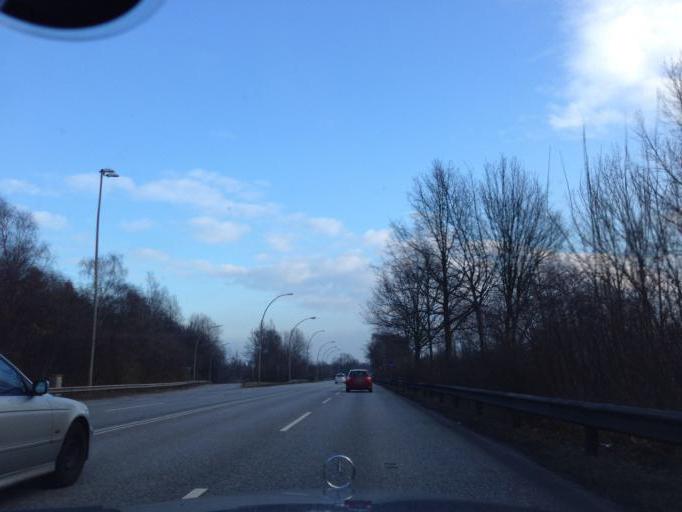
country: DE
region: Schleswig-Holstein
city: Oststeinbek
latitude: 53.5232
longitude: 10.1443
